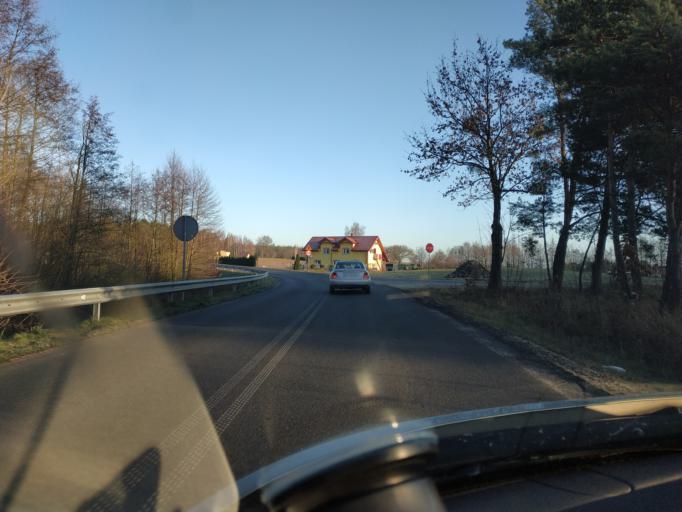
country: PL
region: Kujawsko-Pomorskie
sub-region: Powiat wabrzeski
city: Wabrzezno
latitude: 53.2296
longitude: 18.9545
